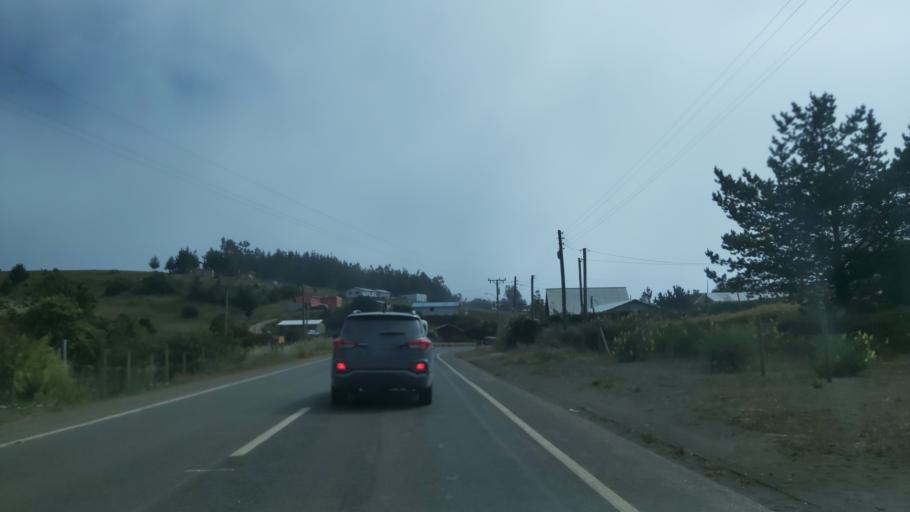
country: CL
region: Maule
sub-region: Provincia de Cauquenes
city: Cauquenes
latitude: -35.8735
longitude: -72.6627
